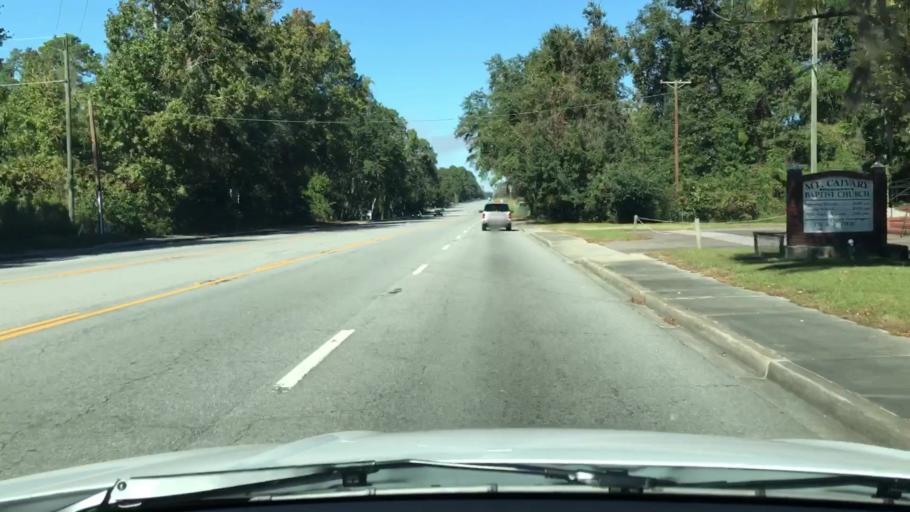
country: US
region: South Carolina
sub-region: Beaufort County
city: Laurel Bay
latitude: 32.5563
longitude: -80.7438
